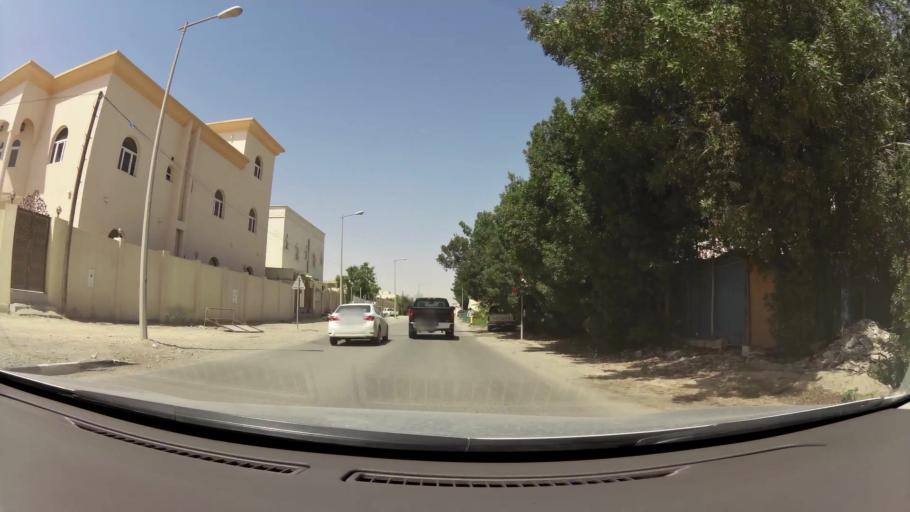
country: QA
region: Baladiyat ar Rayyan
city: Ar Rayyan
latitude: 25.2575
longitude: 51.4123
